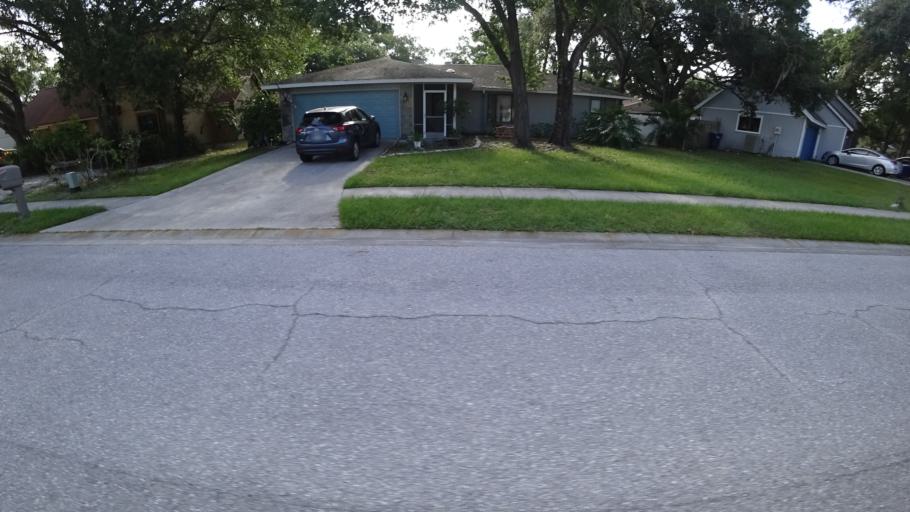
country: US
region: Florida
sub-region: Sarasota County
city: Desoto Lakes
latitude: 27.3897
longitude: -82.5011
